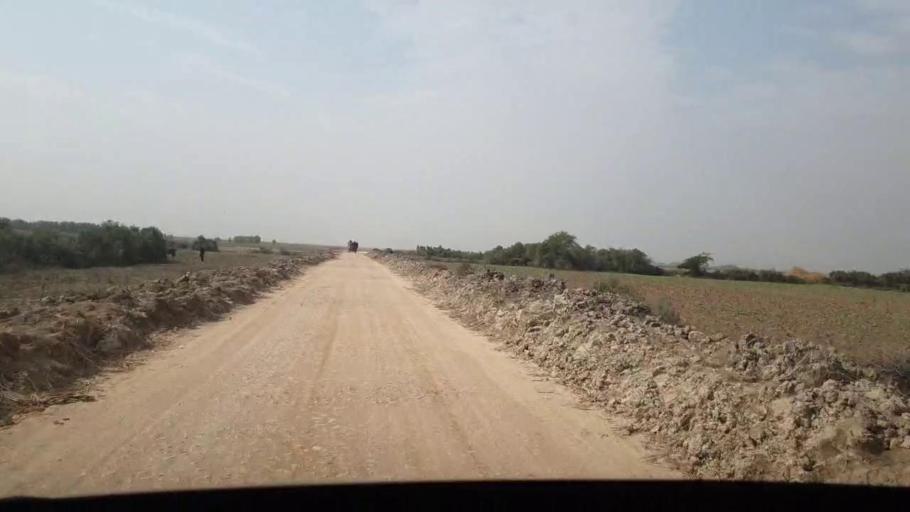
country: PK
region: Sindh
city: Chuhar Jamali
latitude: 24.3628
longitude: 67.9368
